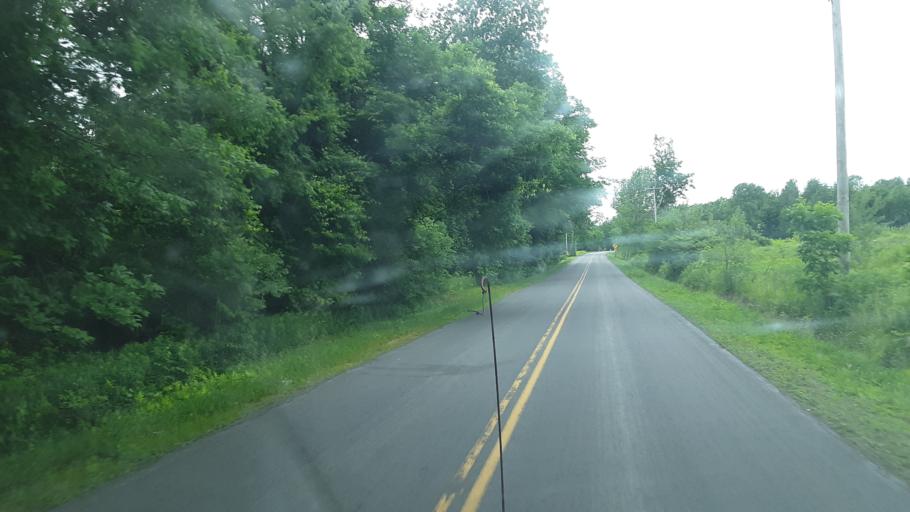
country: US
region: New York
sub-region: Oneida County
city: Rome
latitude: 43.3445
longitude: -75.5540
